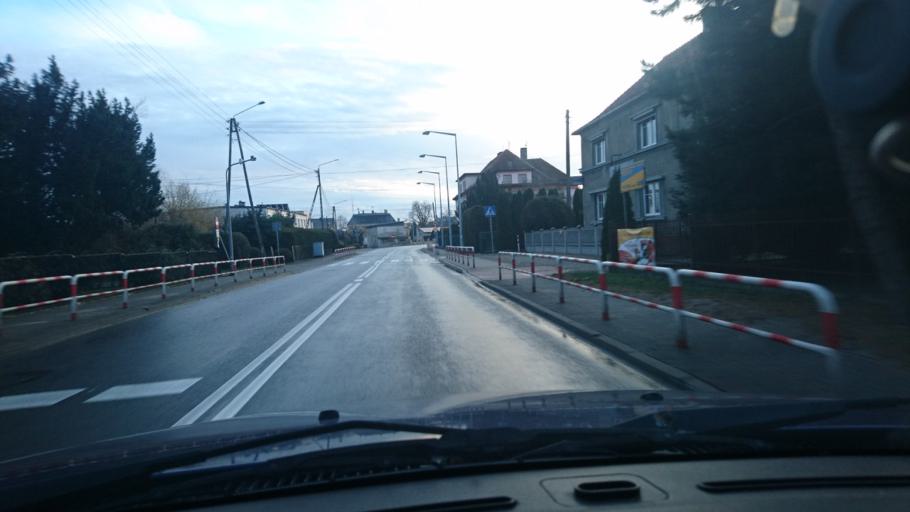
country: PL
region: Opole Voivodeship
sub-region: Powiat kluczborski
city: Byczyna
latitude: 51.1148
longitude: 18.2095
